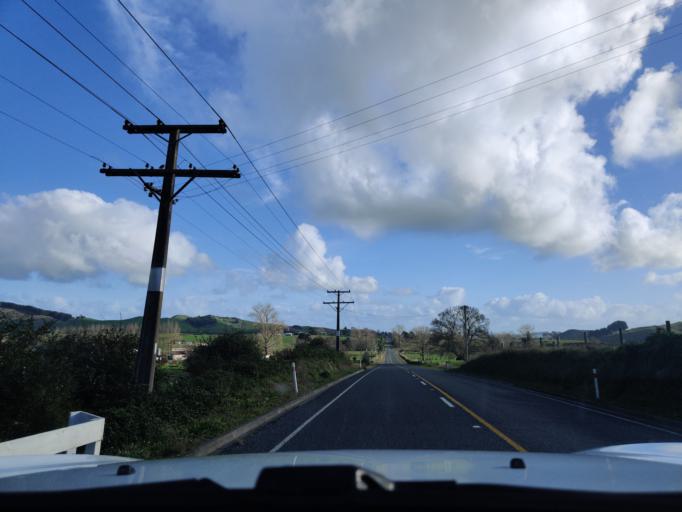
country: NZ
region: Waikato
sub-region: Waikato District
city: Te Kauwhata
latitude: -37.3718
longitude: 175.2375
